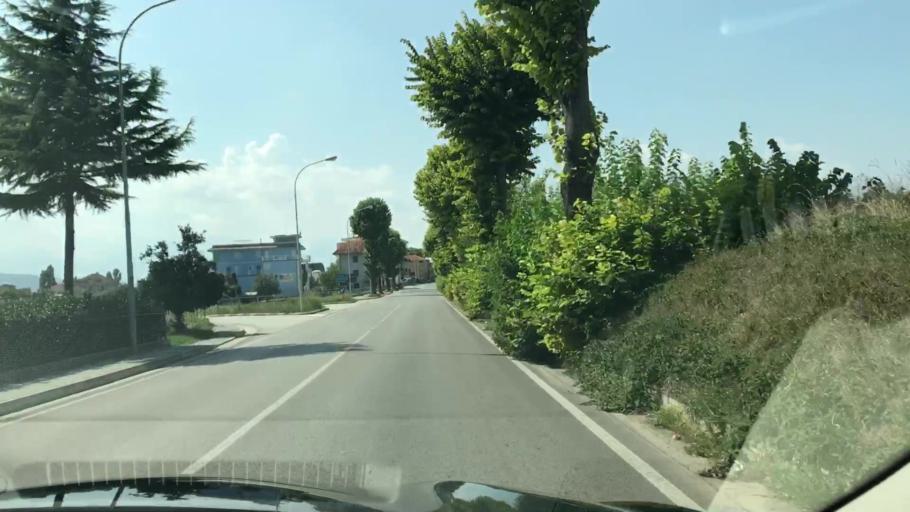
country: IT
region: The Marches
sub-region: Provincia di Ascoli Piceno
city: Stella
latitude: 42.8856
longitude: 13.8058
